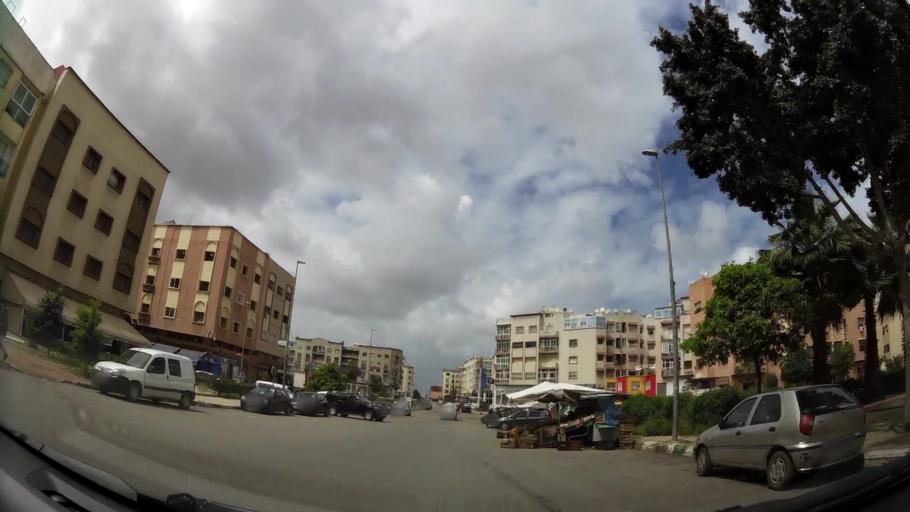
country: MA
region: Grand Casablanca
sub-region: Casablanca
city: Casablanca
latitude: 33.5340
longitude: -7.6089
